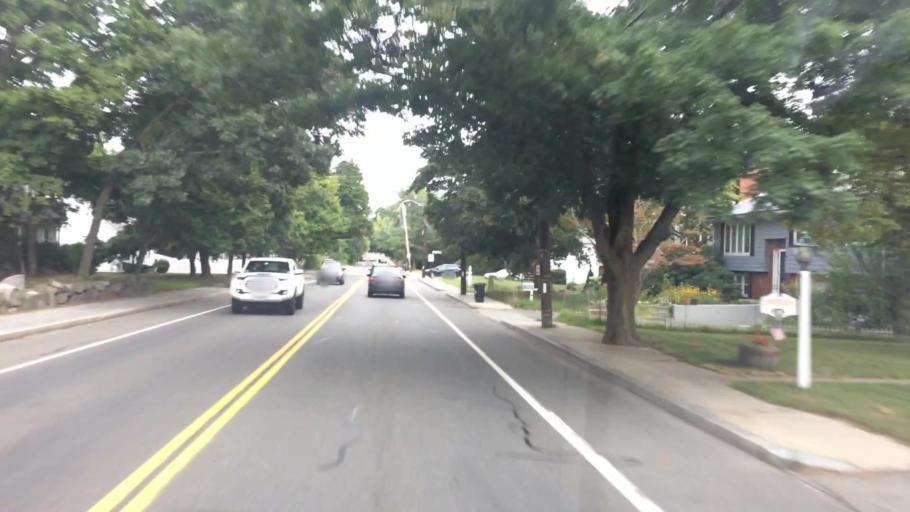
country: US
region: Massachusetts
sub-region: Middlesex County
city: Woburn
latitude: 42.4888
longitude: -71.1698
